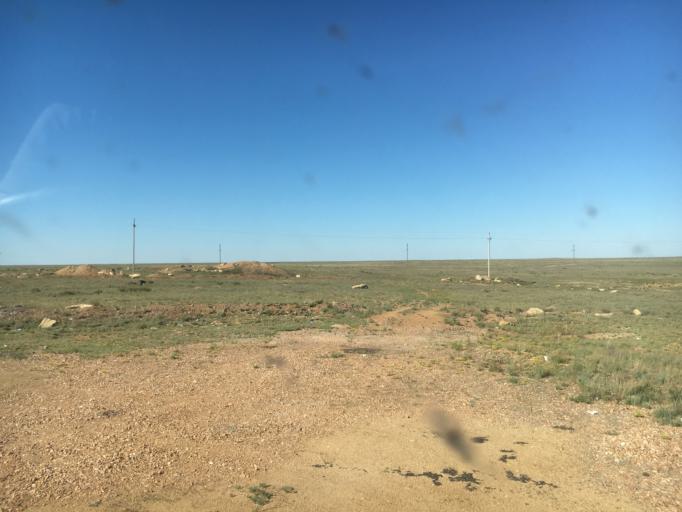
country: RU
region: Orenburg
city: Dombarovskiy
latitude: 50.0822
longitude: 59.5693
